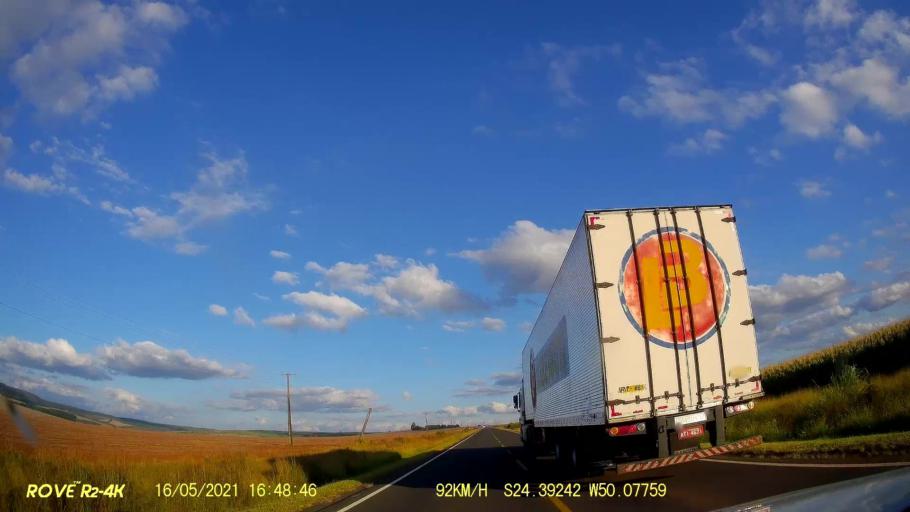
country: BR
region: Parana
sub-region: Pirai Do Sul
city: Pirai do Sul
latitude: -24.3928
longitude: -50.0776
